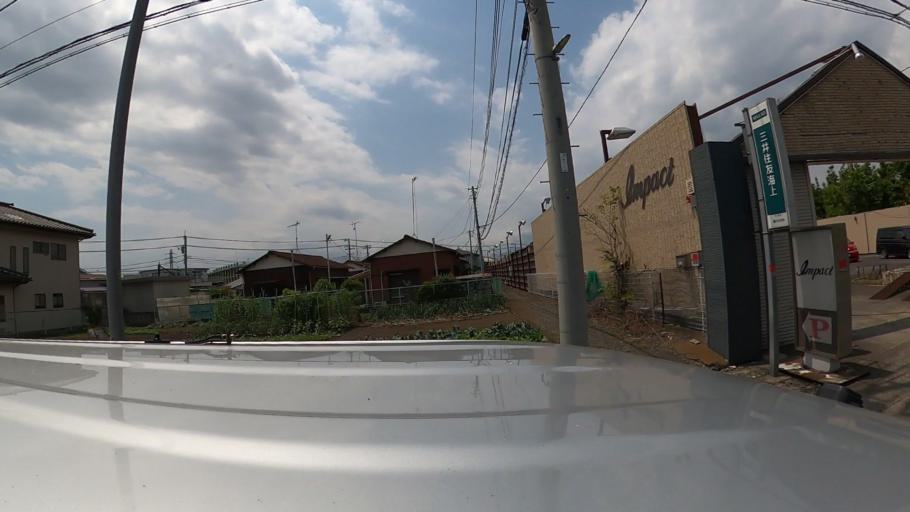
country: JP
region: Kanagawa
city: Chigasaki
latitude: 35.3835
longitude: 139.4014
